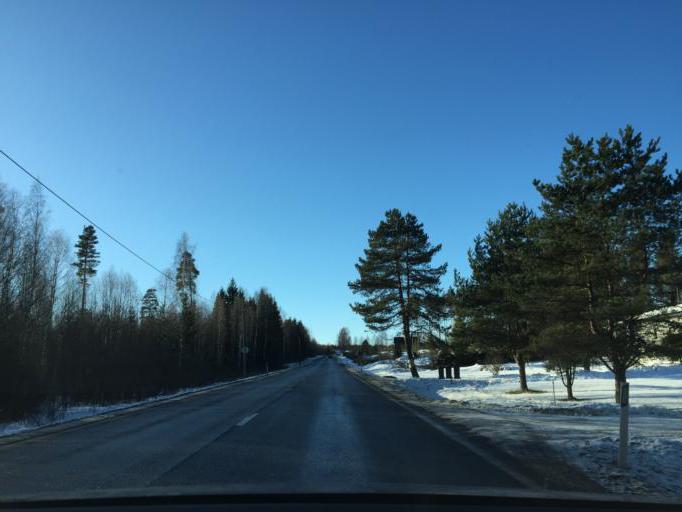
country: NO
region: Akershus
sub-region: Nes
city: Arnes
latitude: 60.1911
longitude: 11.5594
